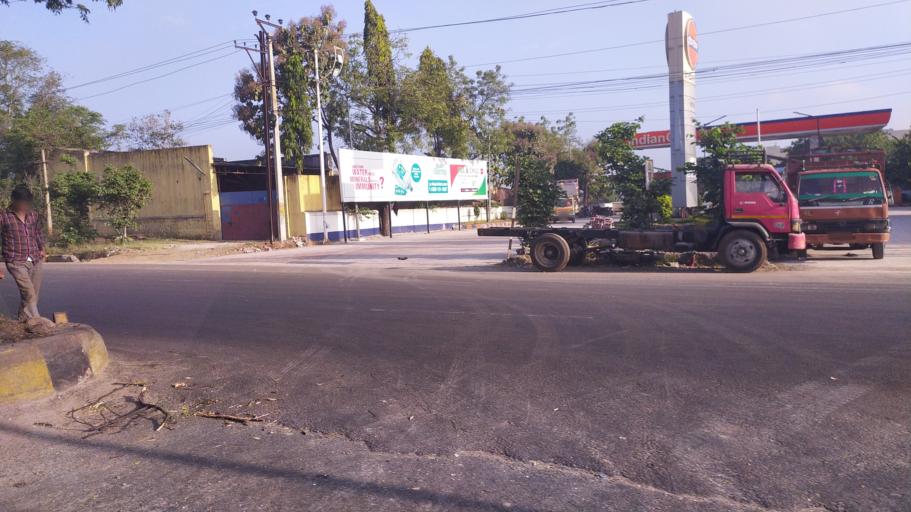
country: IN
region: Telangana
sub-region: Rangareddi
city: Balapur
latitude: 17.3186
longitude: 78.4364
